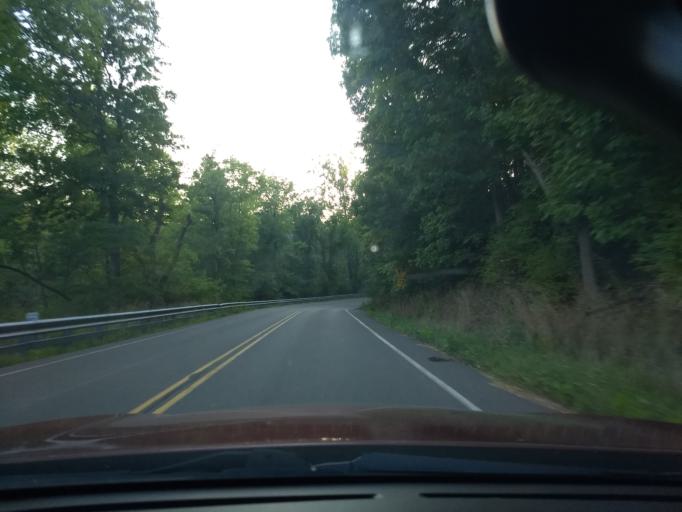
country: US
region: Pennsylvania
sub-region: Allegheny County
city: Bell Acres
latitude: 40.5783
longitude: -80.1546
